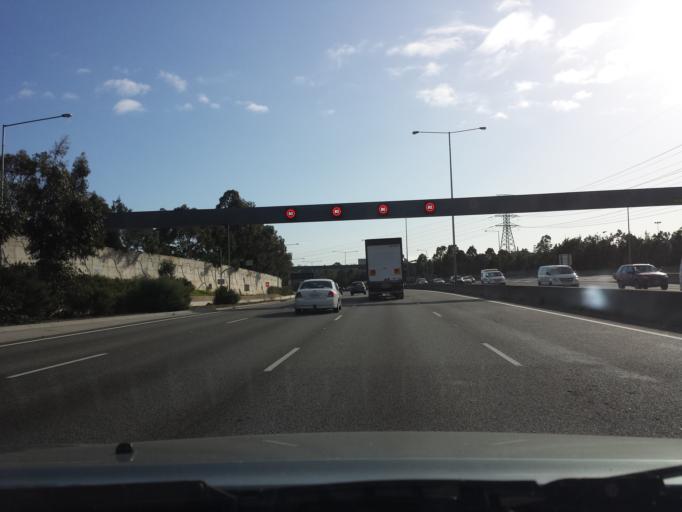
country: AU
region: Victoria
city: Glenferrie
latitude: -37.8431
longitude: 145.0394
